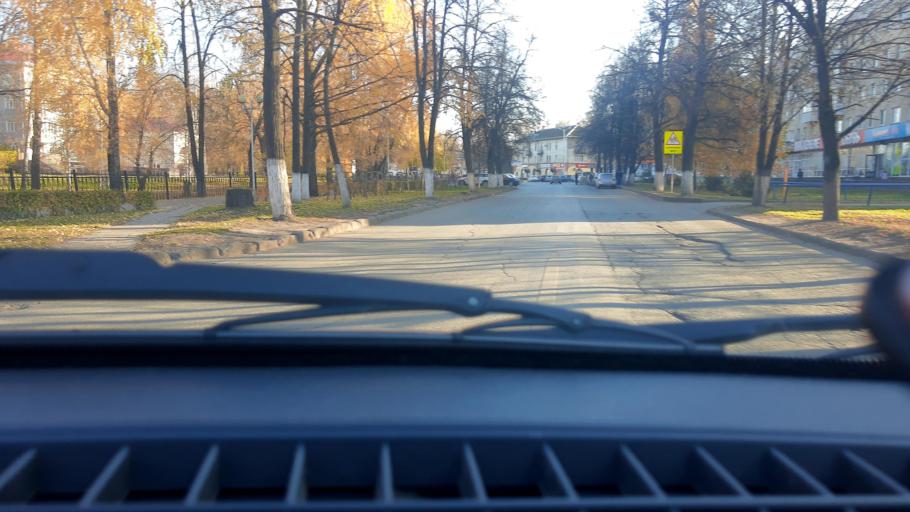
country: RU
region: Bashkortostan
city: Avdon
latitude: 54.7018
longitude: 55.8305
